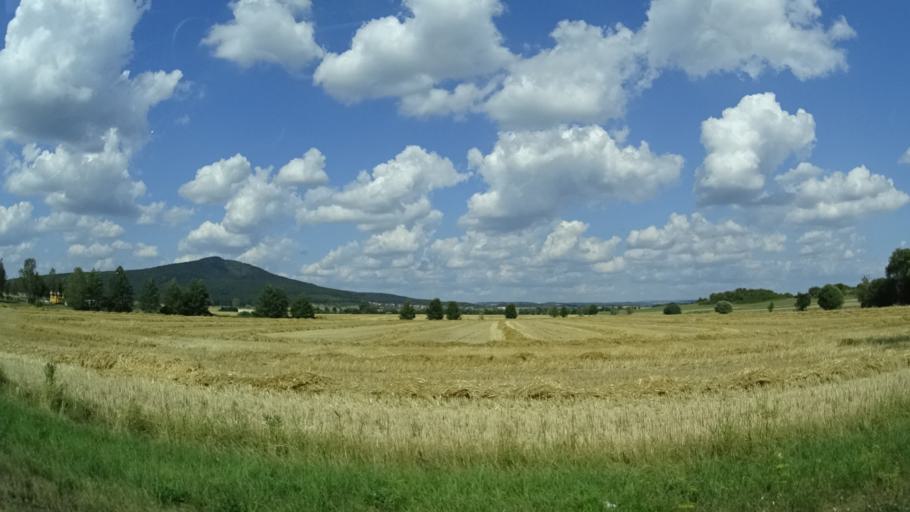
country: DE
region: Bavaria
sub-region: Regierungsbezirk Unterfranken
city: Trappstadt
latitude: 50.3486
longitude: 10.5736
